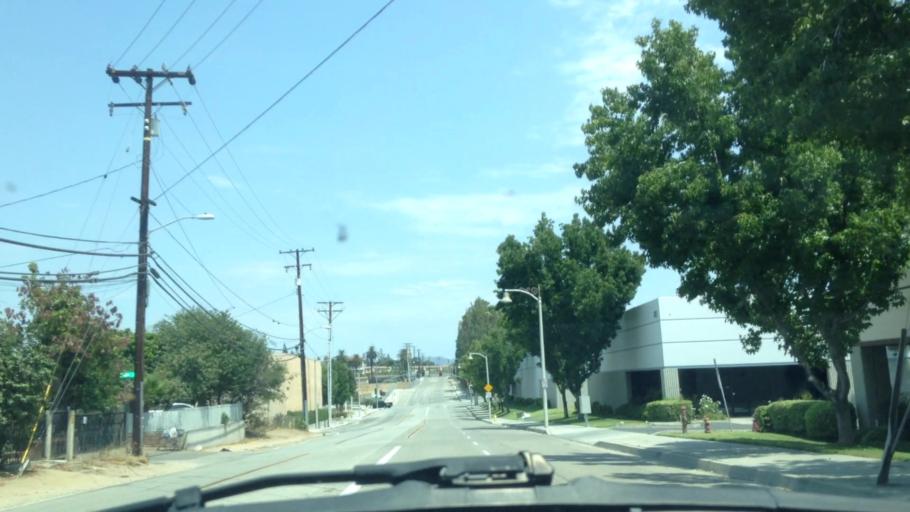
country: US
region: California
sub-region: Orange County
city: Placentia
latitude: 33.8668
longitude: -117.8763
